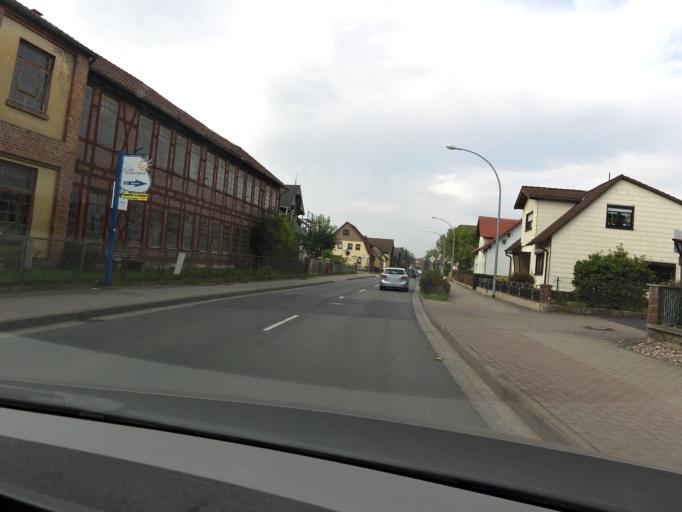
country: DE
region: Thuringia
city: Barchfeld
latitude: 50.7949
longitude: 10.3012
